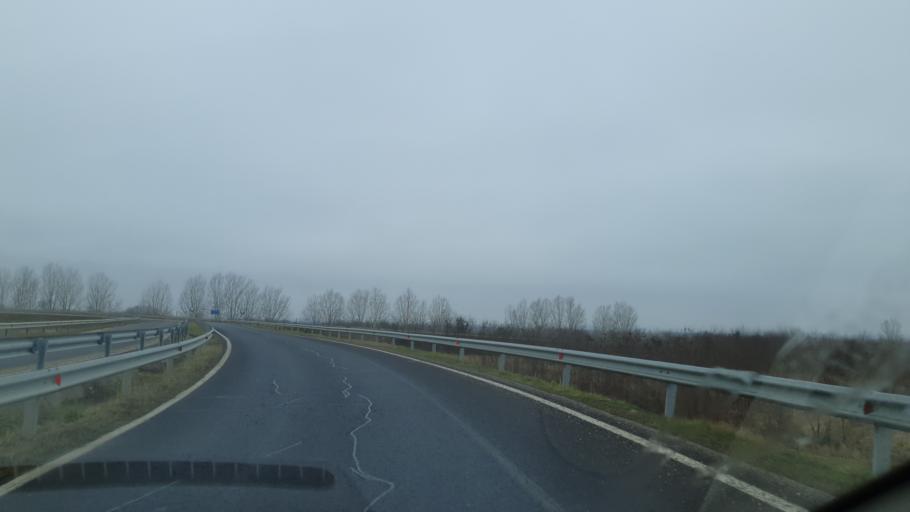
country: HU
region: Borsod-Abauj-Zemplen
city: Hejobaba
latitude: 47.8811
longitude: 20.9011
